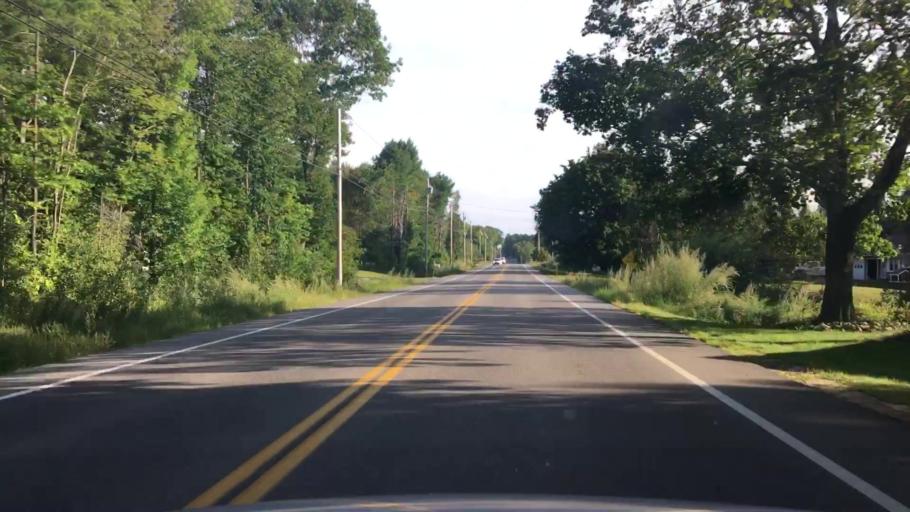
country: US
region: Maine
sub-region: Cumberland County
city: South Windham
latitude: 43.7823
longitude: -70.4397
